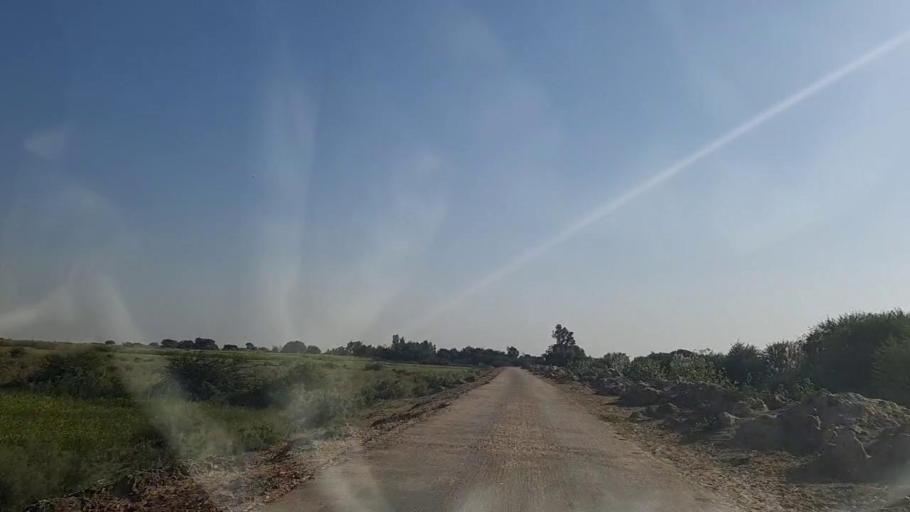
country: PK
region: Sindh
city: Mirpur Batoro
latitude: 24.5560
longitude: 68.1717
